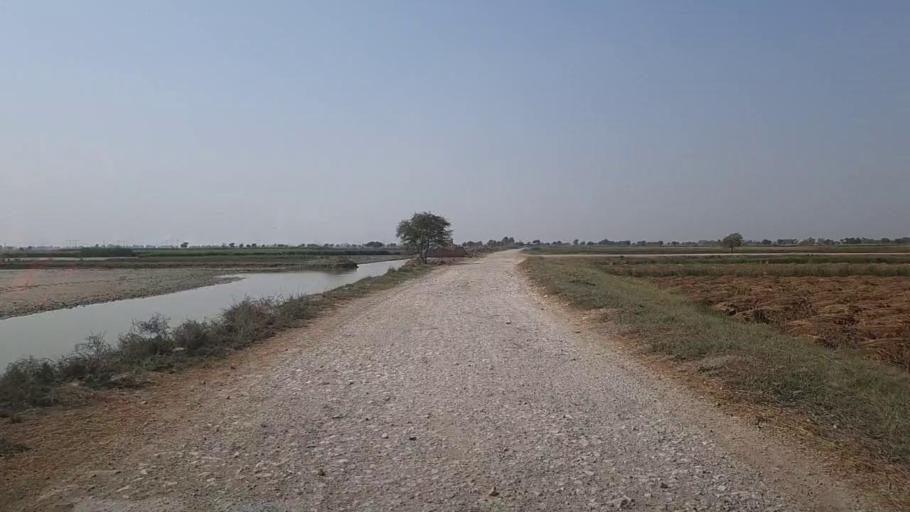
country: PK
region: Sindh
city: Kandhkot
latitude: 28.3927
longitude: 69.3104
